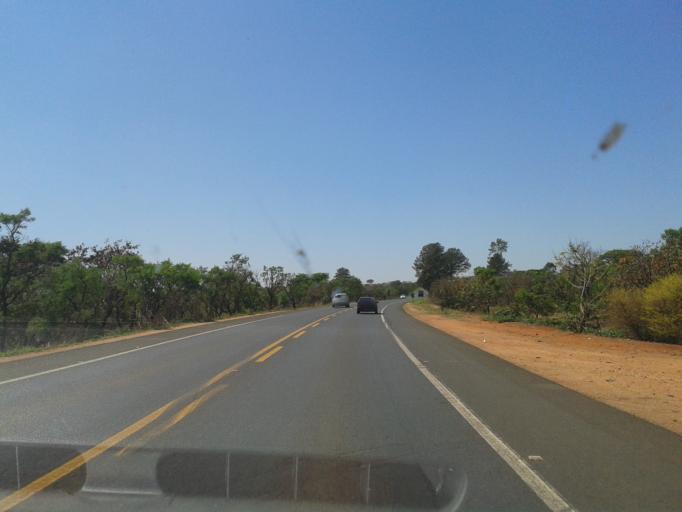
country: BR
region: Minas Gerais
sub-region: Uberaba
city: Uberaba
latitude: -19.2911
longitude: -47.6029
